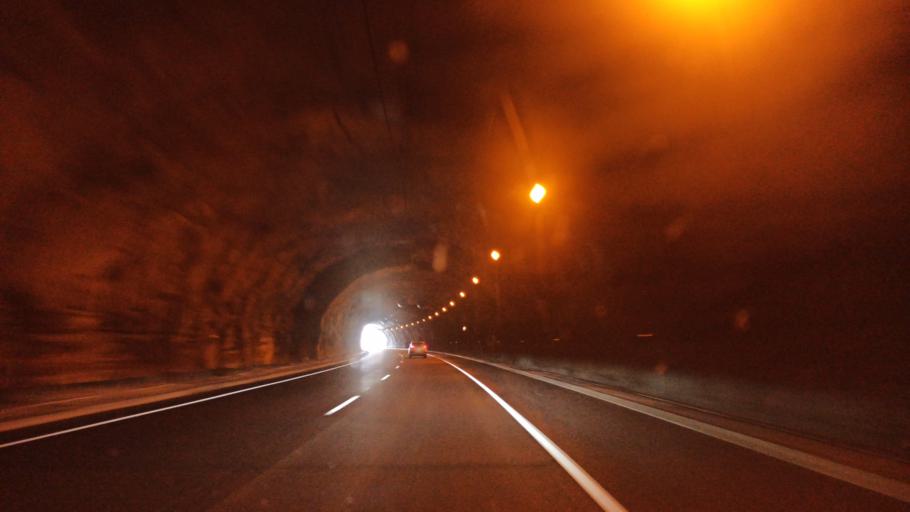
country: ES
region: Catalonia
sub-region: Provincia de Barcelona
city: Sant Pere de Ribes
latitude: 41.2725
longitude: 1.7343
